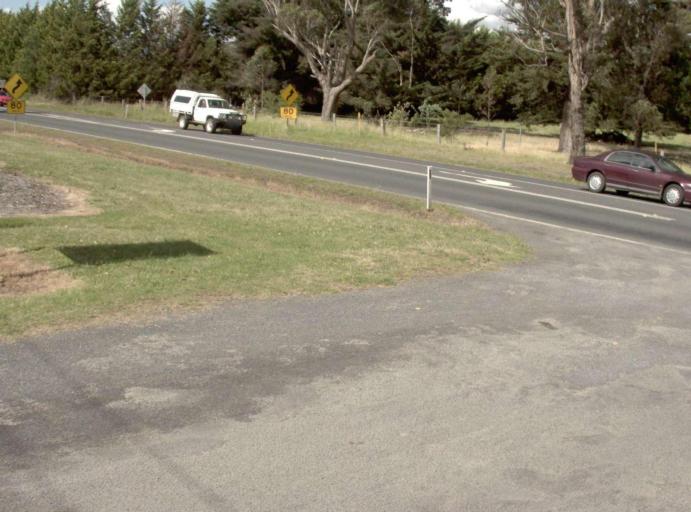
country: AU
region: Victoria
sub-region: Latrobe
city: Morwell
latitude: -38.2975
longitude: 146.4224
